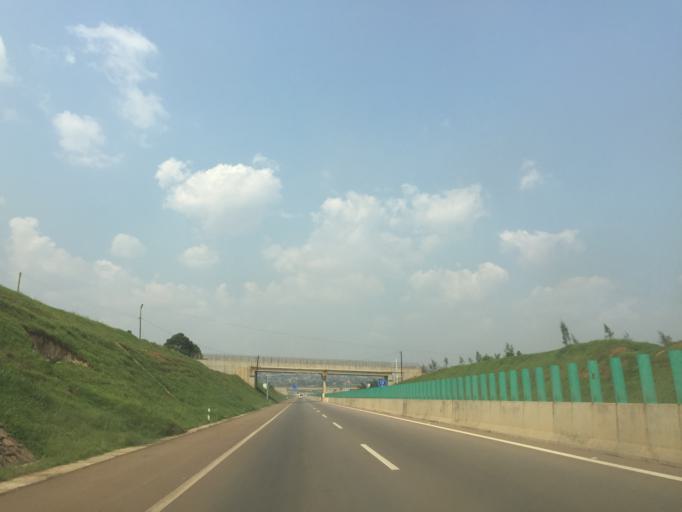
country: UG
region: Central Region
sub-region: Wakiso District
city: Kajansi
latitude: 0.2040
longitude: 32.5277
